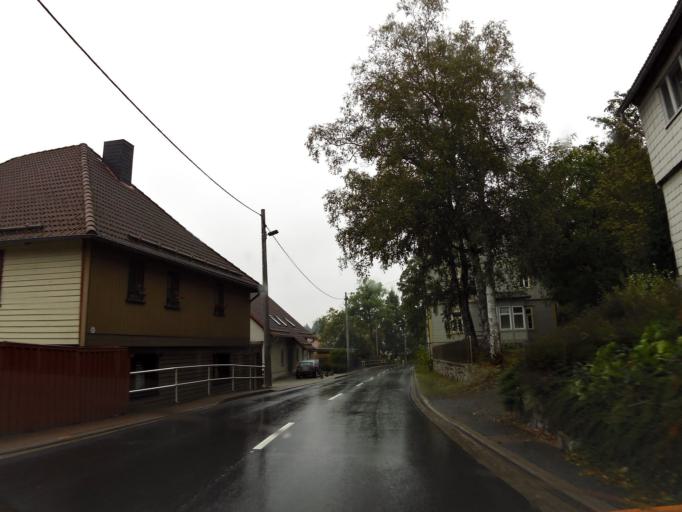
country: DE
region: Saxony-Anhalt
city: Hasselfelde
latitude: 51.6663
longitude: 10.8903
